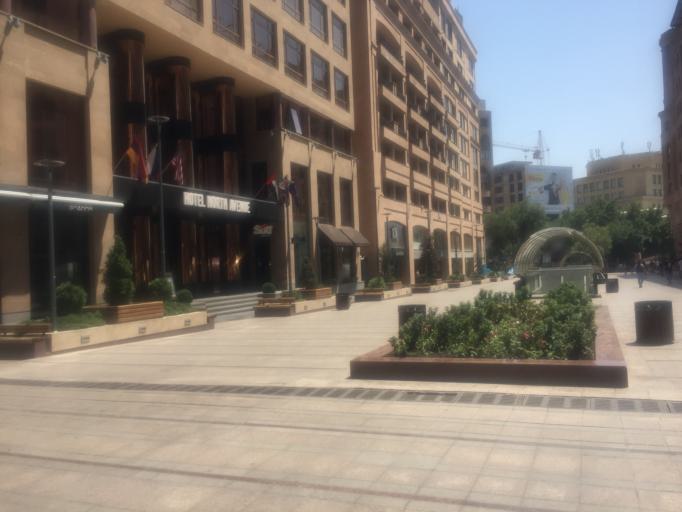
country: AM
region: Yerevan
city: Yerevan
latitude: 40.1811
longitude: 44.5145
